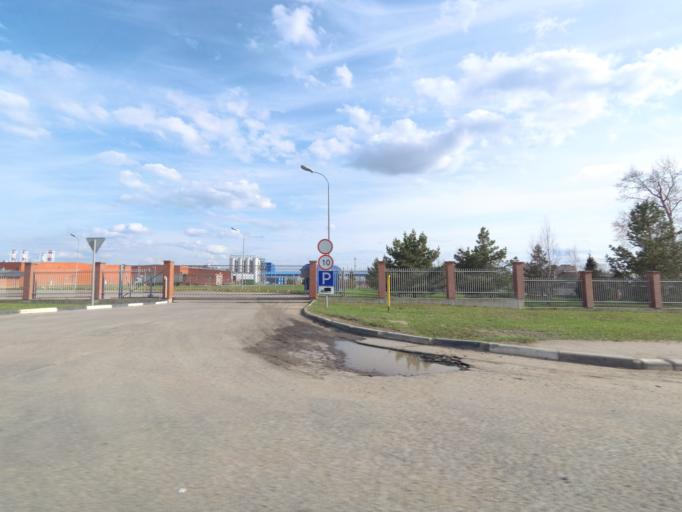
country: RU
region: Moskovskaya
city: Lobnya
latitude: 56.0251
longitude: 37.4314
